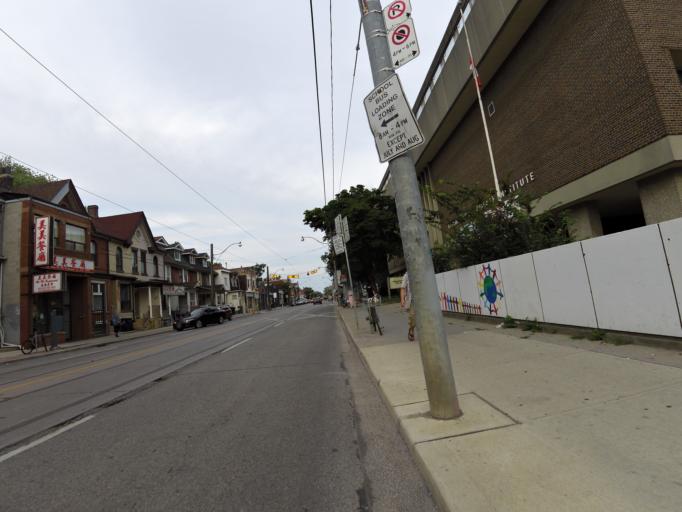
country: CA
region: Ontario
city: Toronto
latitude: 43.6662
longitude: -79.3492
